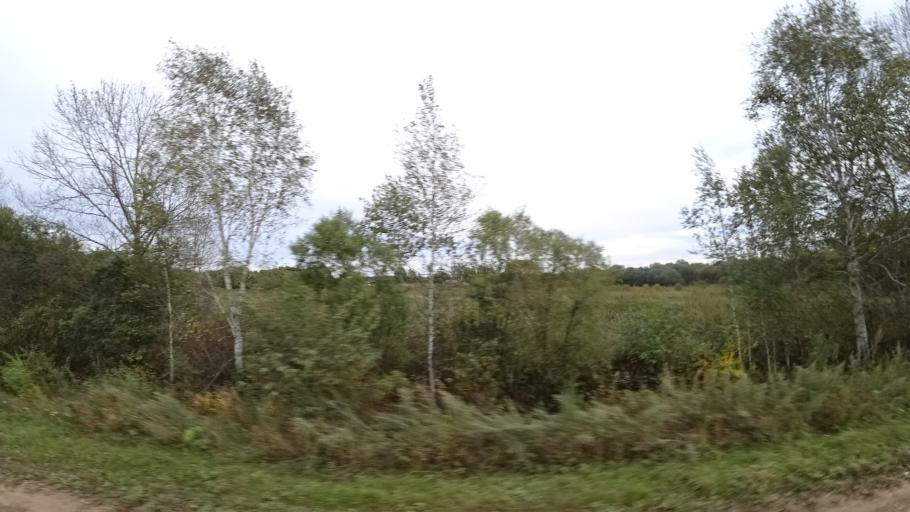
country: RU
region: Amur
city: Arkhara
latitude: 49.4328
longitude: 130.2534
